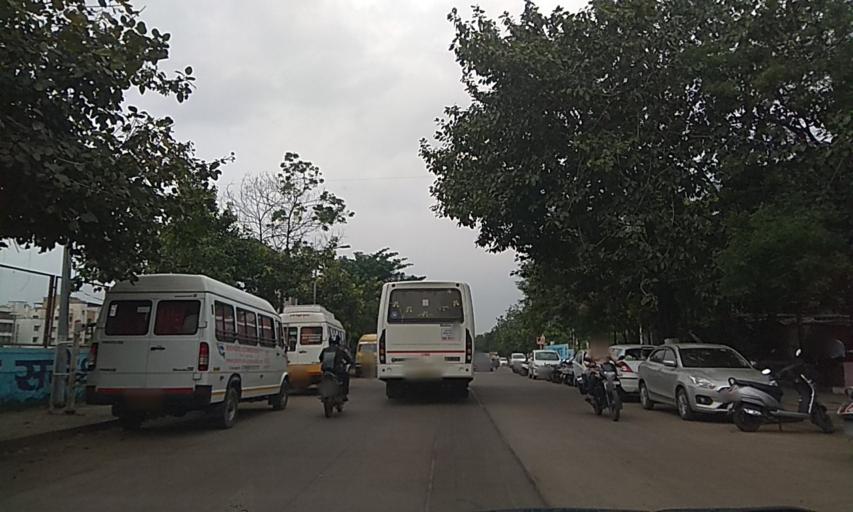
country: IN
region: Maharashtra
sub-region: Pune Division
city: Lohogaon
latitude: 18.5651
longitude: 73.9095
